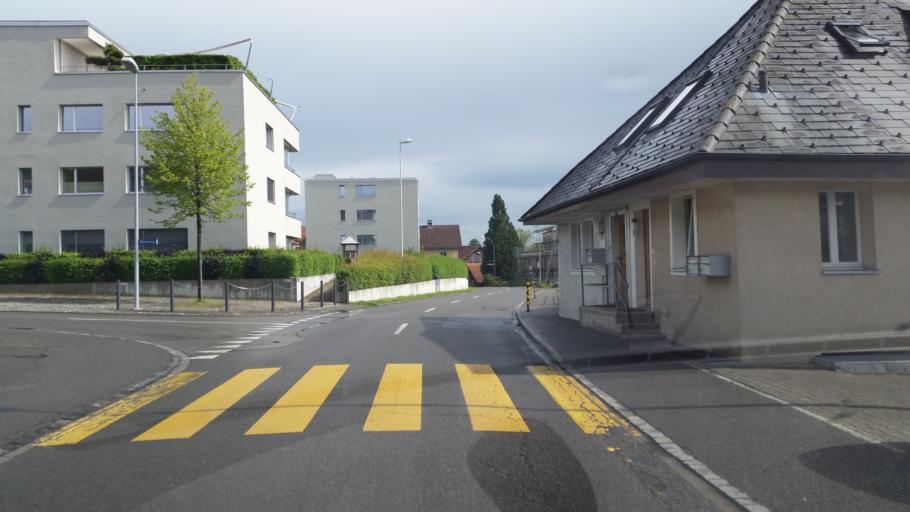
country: CH
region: Aargau
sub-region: Bezirk Lenzburg
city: Seengen
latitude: 47.3248
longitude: 8.2070
